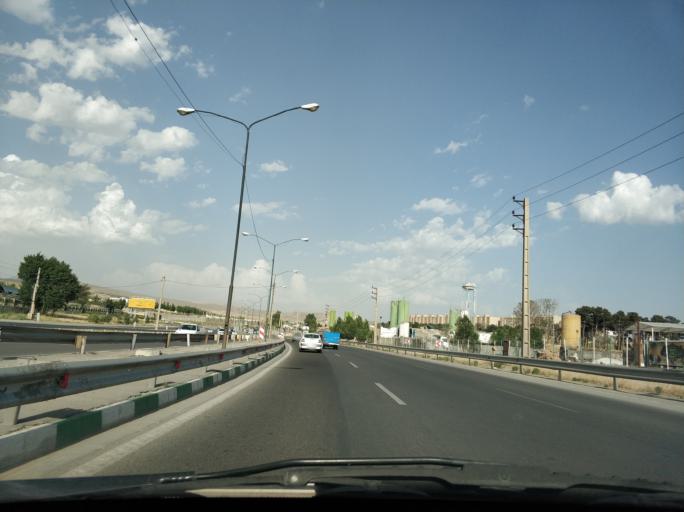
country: IR
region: Tehran
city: Tajrish
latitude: 35.7482
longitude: 51.5884
